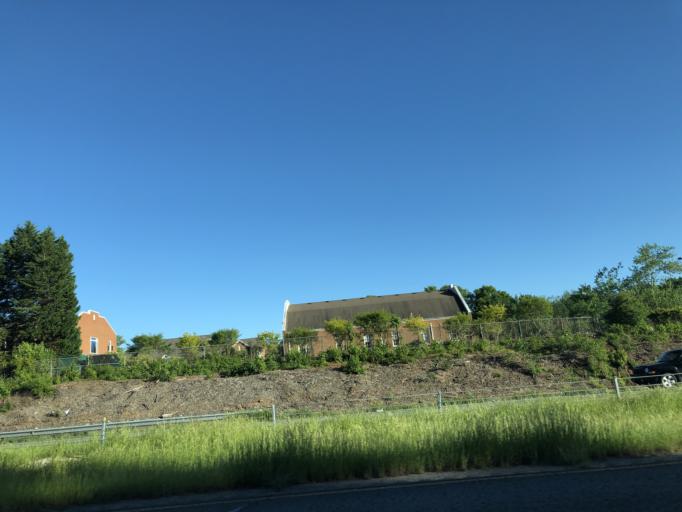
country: US
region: Georgia
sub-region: Clarke County
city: Country Club Estates
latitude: 33.9708
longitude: -83.4169
